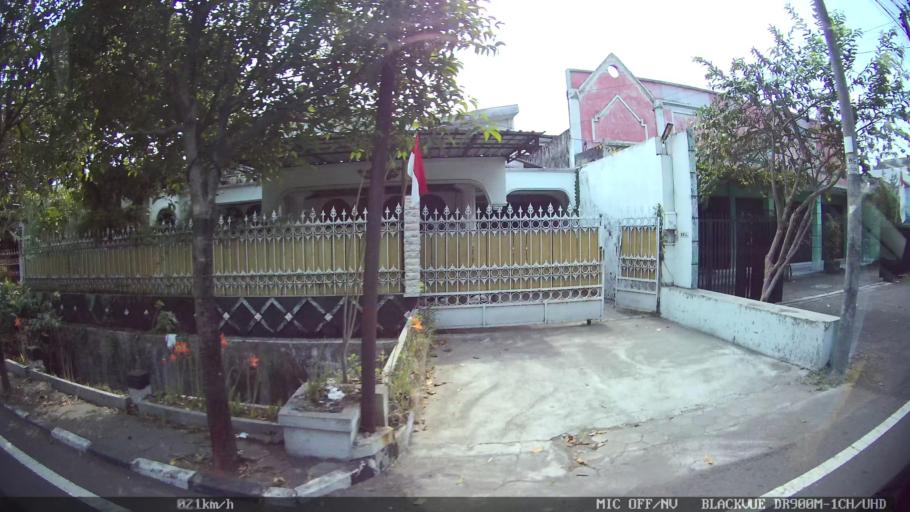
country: ID
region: Daerah Istimewa Yogyakarta
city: Yogyakarta
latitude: -7.8184
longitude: 110.3926
